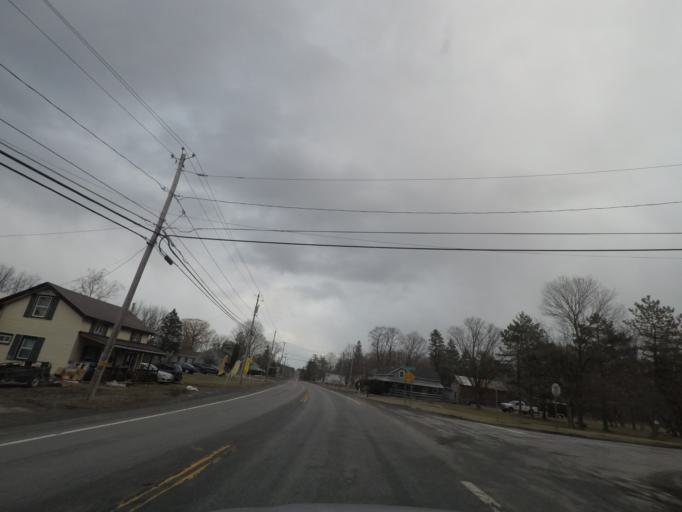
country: US
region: New York
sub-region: Madison County
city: Chittenango
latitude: 43.0542
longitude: -75.8479
